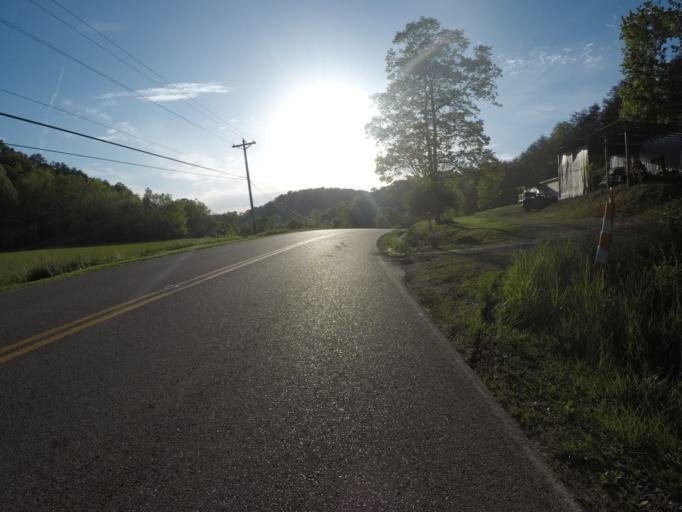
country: US
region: West Virginia
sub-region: Cabell County
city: Huntington
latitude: 38.5549
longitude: -82.4501
